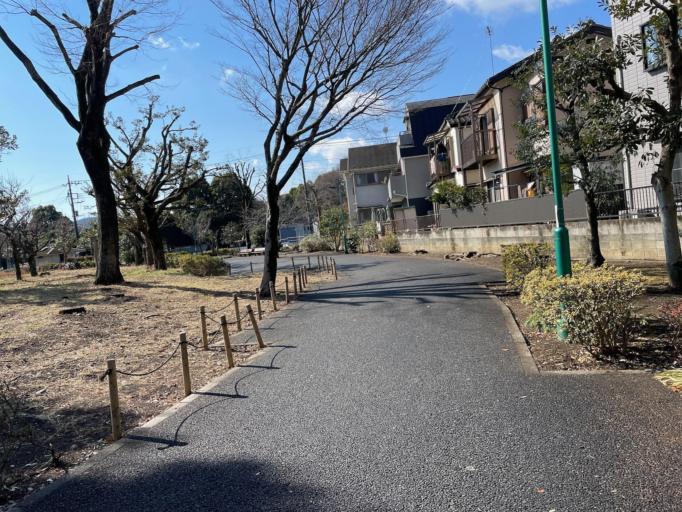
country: JP
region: Tokyo
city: Kokubunji
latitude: 35.6572
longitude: 139.4744
